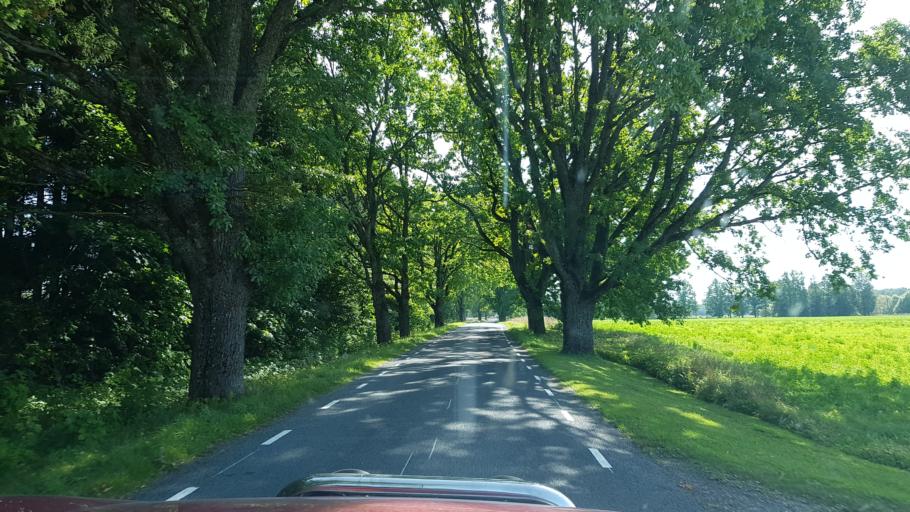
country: EE
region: Viljandimaa
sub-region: Suure-Jaani vald
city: Suure-Jaani
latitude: 58.4831
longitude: 25.5201
